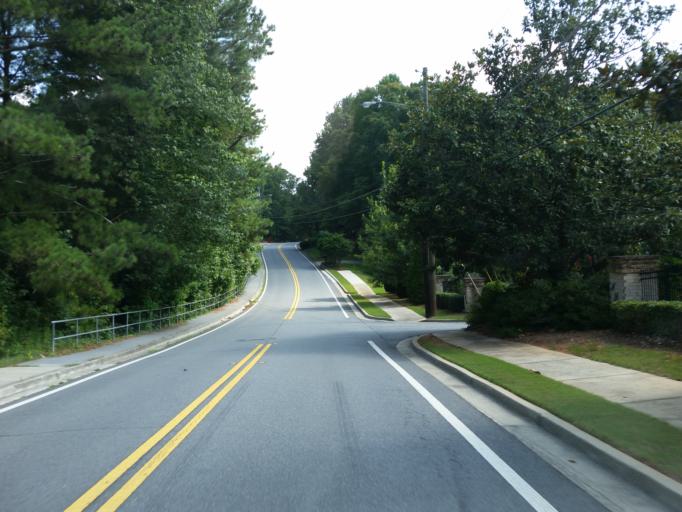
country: US
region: Georgia
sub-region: Fulton County
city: Roswell
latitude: 34.0307
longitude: -84.4425
